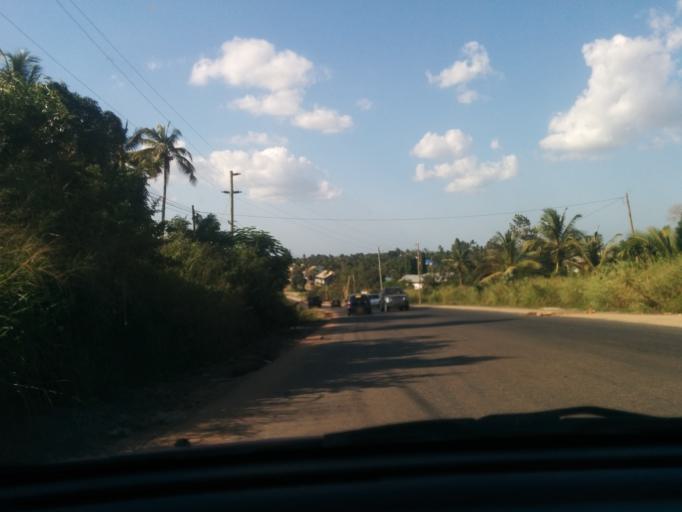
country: TZ
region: Dar es Salaam
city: Magomeni
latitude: -6.7588
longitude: 39.1249
